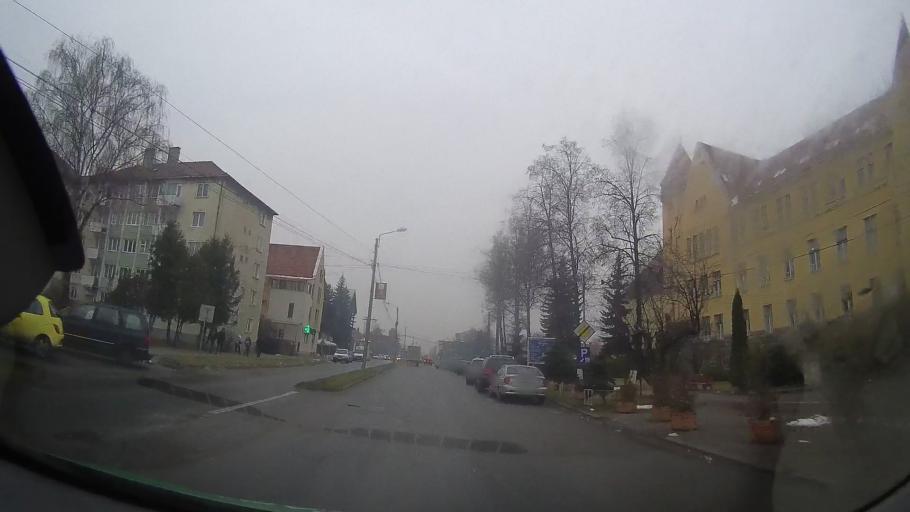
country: RO
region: Harghita
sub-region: Municipiul Gheorgheni
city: Gheorgheni
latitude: 46.7235
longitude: 25.6005
